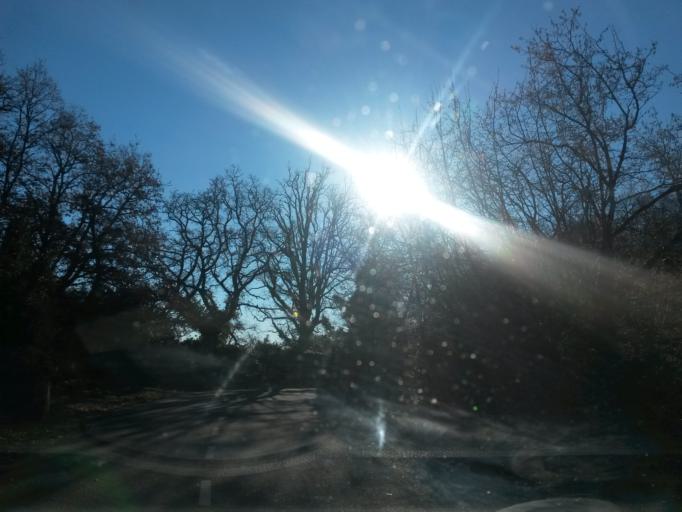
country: ES
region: Catalonia
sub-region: Provincia de Girona
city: les Planes d'Hostoles
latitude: 42.0227
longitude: 2.5362
